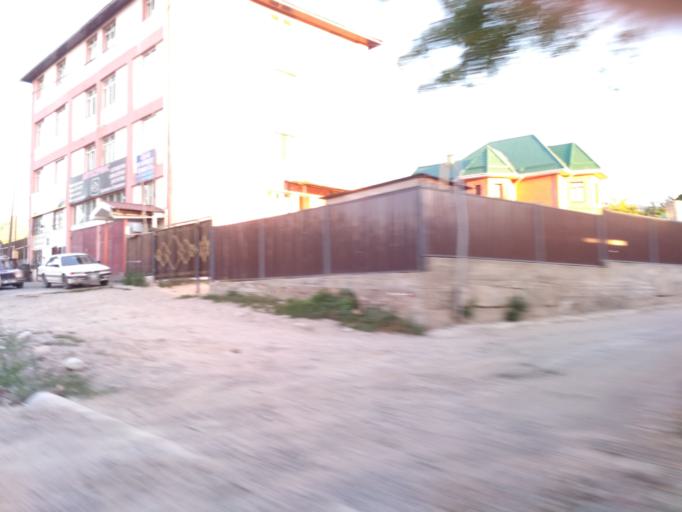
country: KZ
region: Almaty Qalasy
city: Almaty
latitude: 43.1727
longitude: 76.7690
